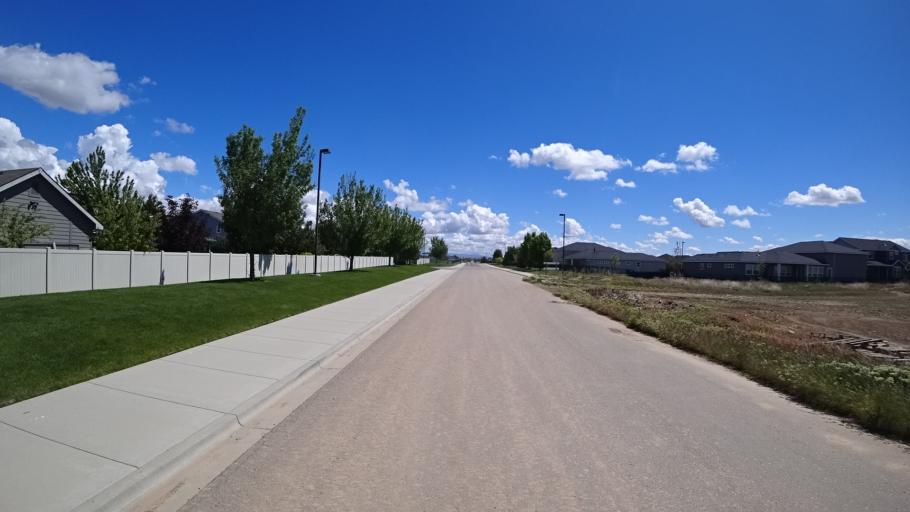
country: US
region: Idaho
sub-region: Ada County
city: Kuna
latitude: 43.5102
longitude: -116.4292
